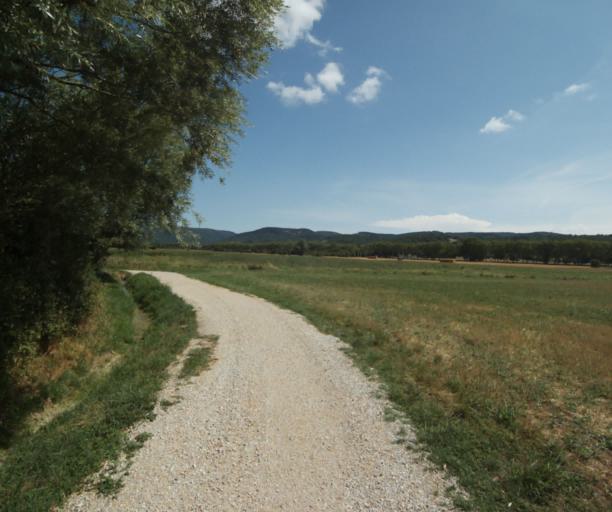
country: FR
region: Midi-Pyrenees
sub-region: Departement de la Haute-Garonne
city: Revel
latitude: 43.4575
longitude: 2.0203
